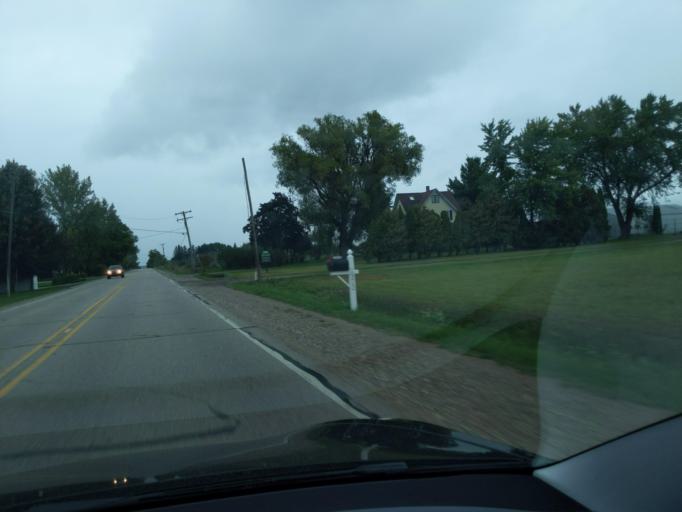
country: US
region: Michigan
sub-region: Antrim County
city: Elk Rapids
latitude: 44.8341
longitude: -85.4050
